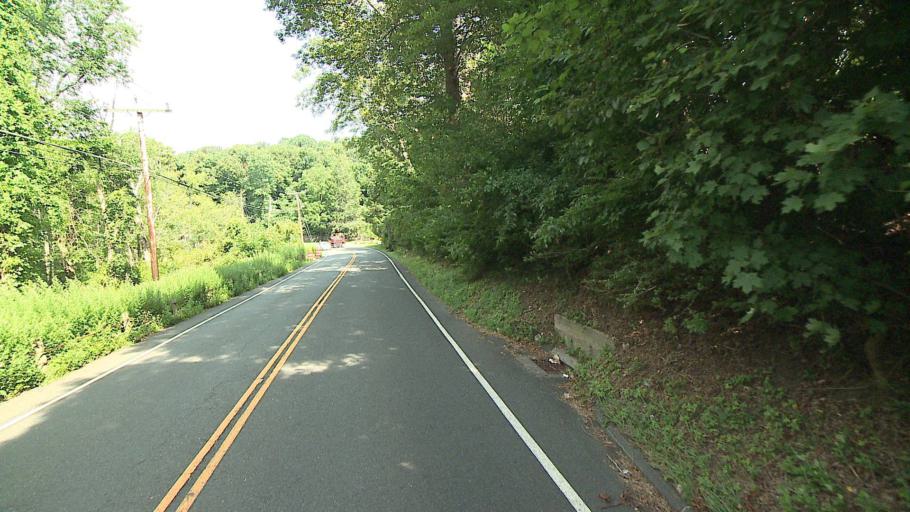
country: US
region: New York
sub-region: Putnam County
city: Putnam Lake
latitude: 41.4438
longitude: -73.5074
